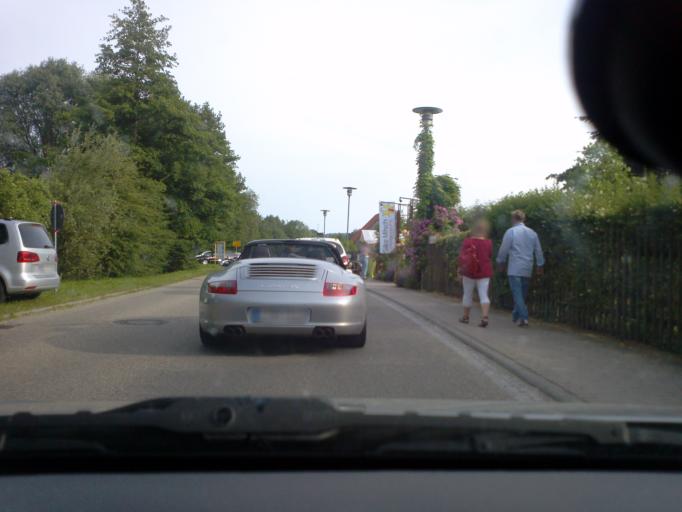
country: DE
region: Baden-Wuerttemberg
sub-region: Karlsruhe Region
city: Sternenfels
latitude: 49.0251
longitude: 8.8542
